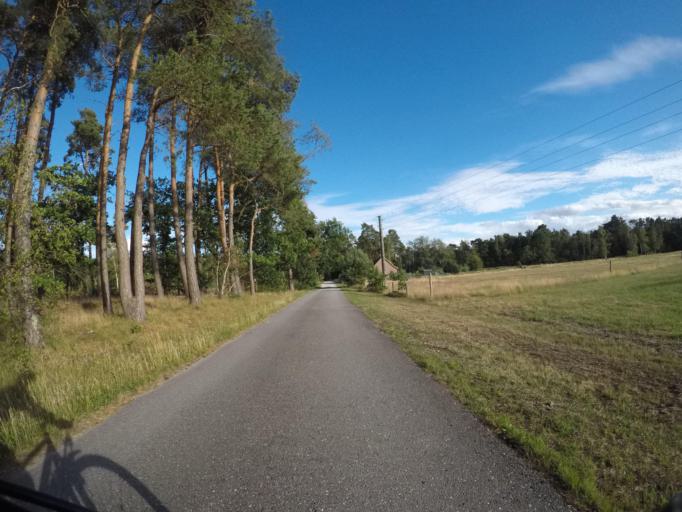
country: DE
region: Mecklenburg-Vorpommern
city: Lubtheen
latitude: 53.2331
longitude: 11.0445
